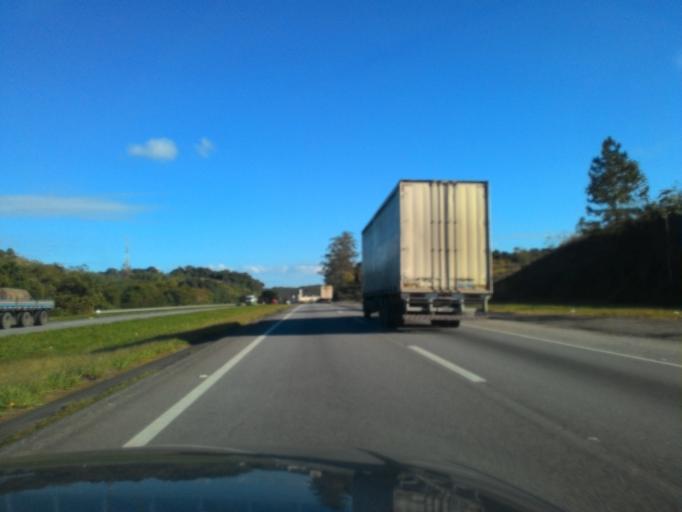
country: BR
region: Sao Paulo
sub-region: Registro
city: Registro
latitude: -24.5525
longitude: -47.8645
